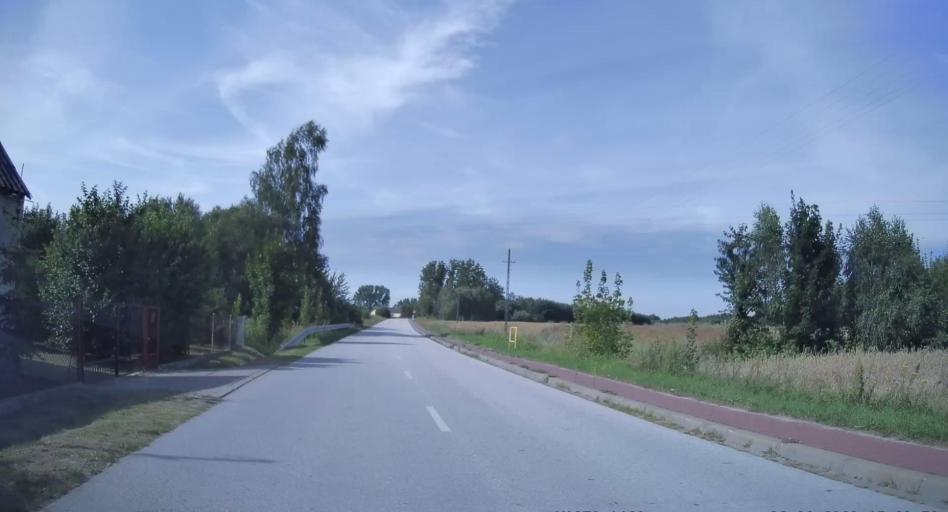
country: PL
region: Lodz Voivodeship
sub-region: Powiat opoczynski
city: Mniszkow
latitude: 51.3455
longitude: 20.0387
